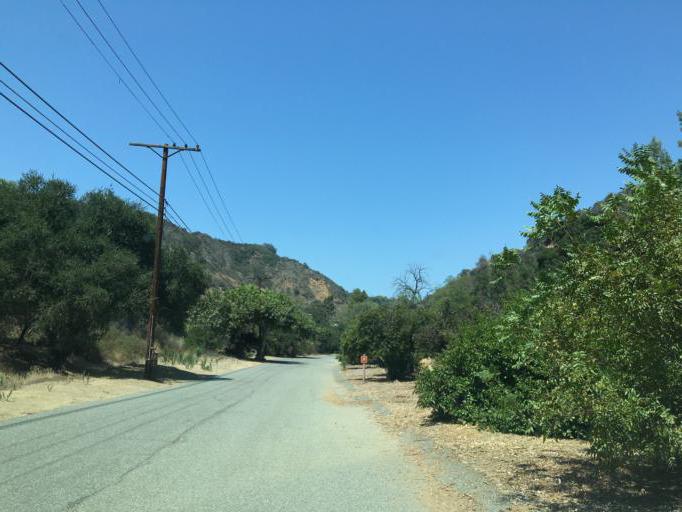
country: US
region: California
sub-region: Los Angeles County
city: Beverly Hills
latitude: 34.1064
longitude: -118.4153
